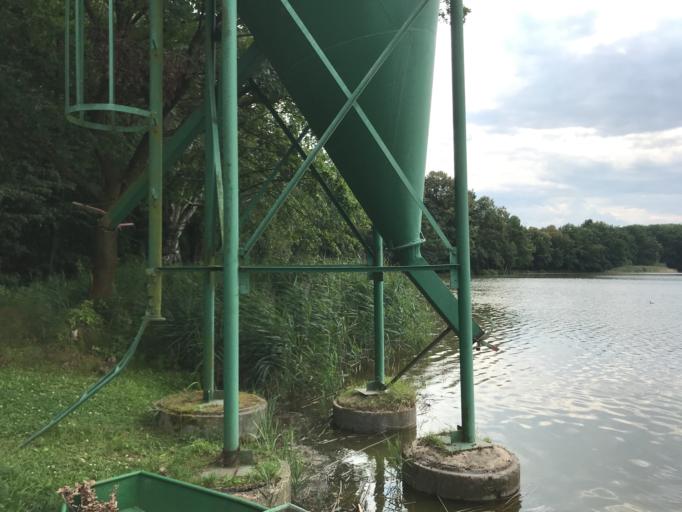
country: CZ
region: Jihocesky
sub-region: Okres Jindrichuv Hradec
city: Lomnice nad Luznici
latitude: 49.0934
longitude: 14.7131
